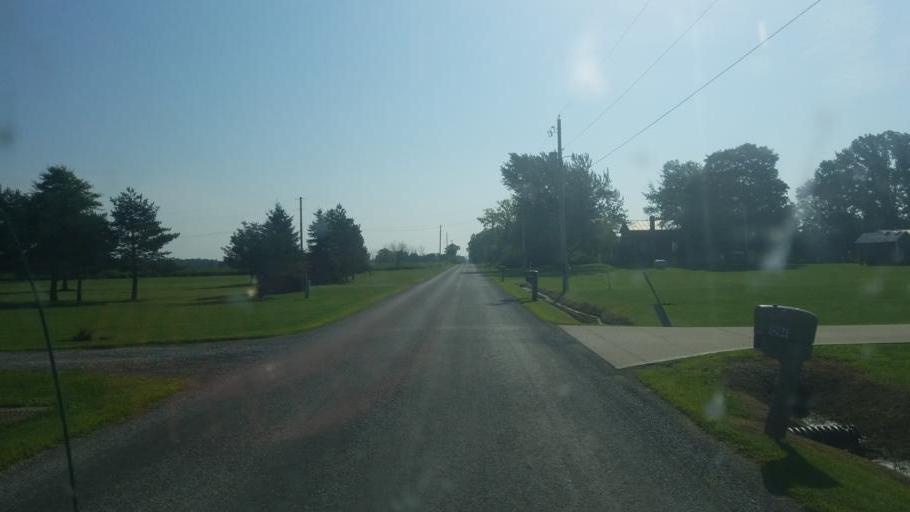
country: US
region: Ohio
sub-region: Lorain County
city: Wellington
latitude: 41.0858
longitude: -82.1572
